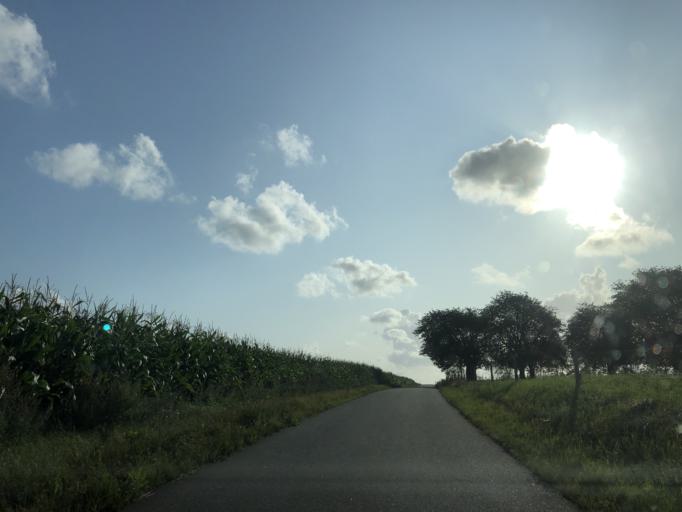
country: DK
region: Central Jutland
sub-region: Favrskov Kommune
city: Hammel
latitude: 56.2428
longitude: 9.7686
